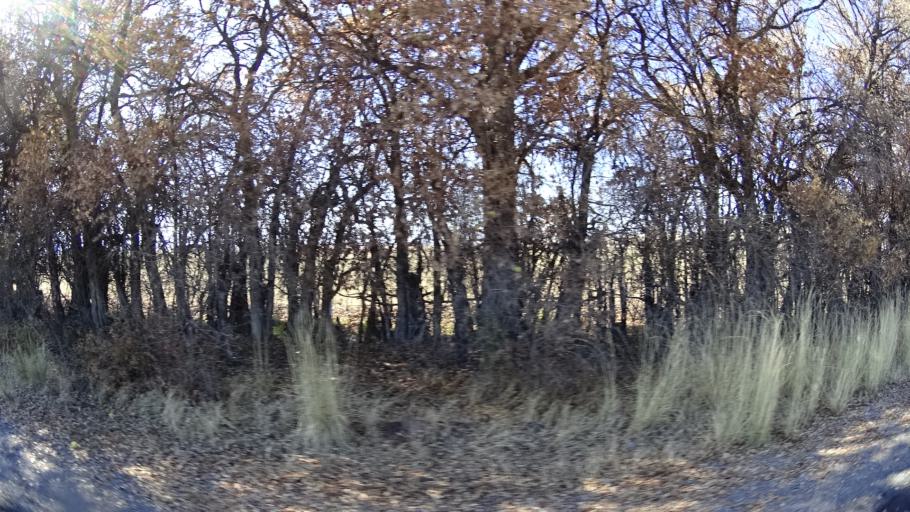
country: US
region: California
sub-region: Siskiyou County
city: Montague
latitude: 41.7231
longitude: -122.3892
